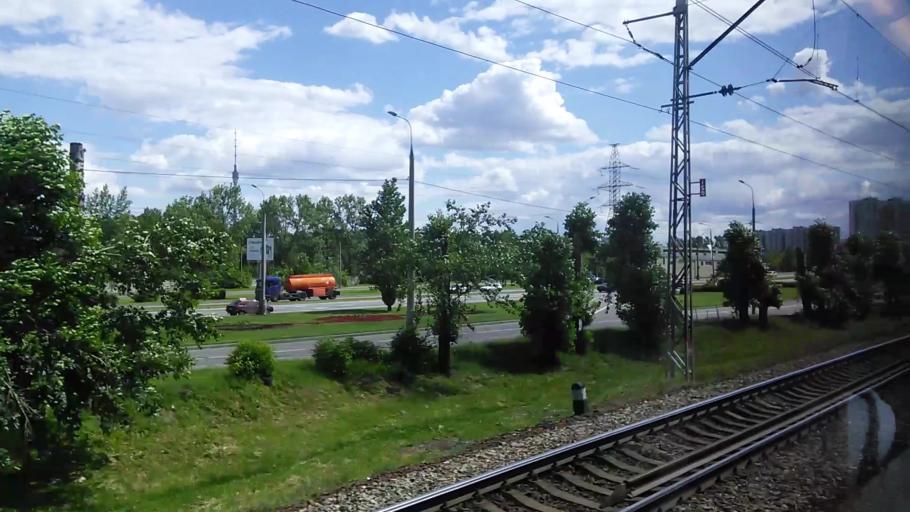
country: RU
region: Moscow
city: Novovladykino
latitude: 55.8378
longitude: 37.5789
